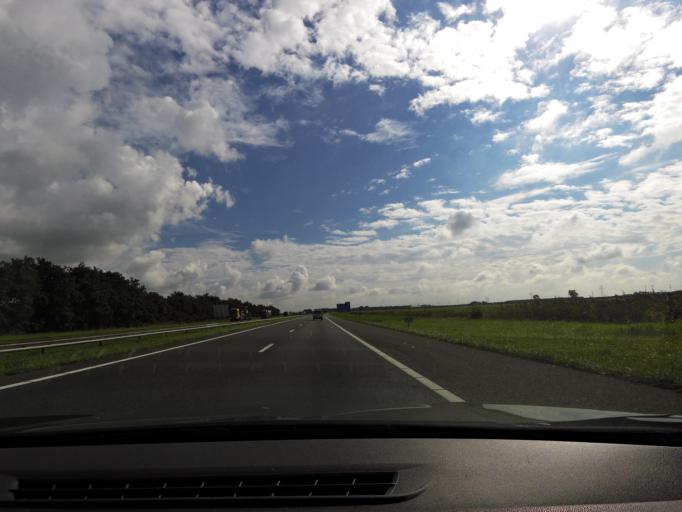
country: NL
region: Zeeland
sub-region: Gemeente Goes
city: Goes
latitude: 51.4791
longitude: 3.9149
